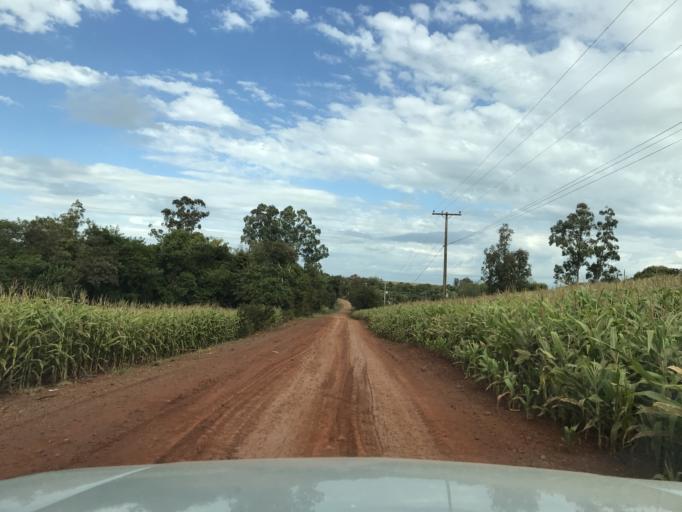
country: BR
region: Parana
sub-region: Palotina
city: Palotina
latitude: -24.3207
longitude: -53.8064
